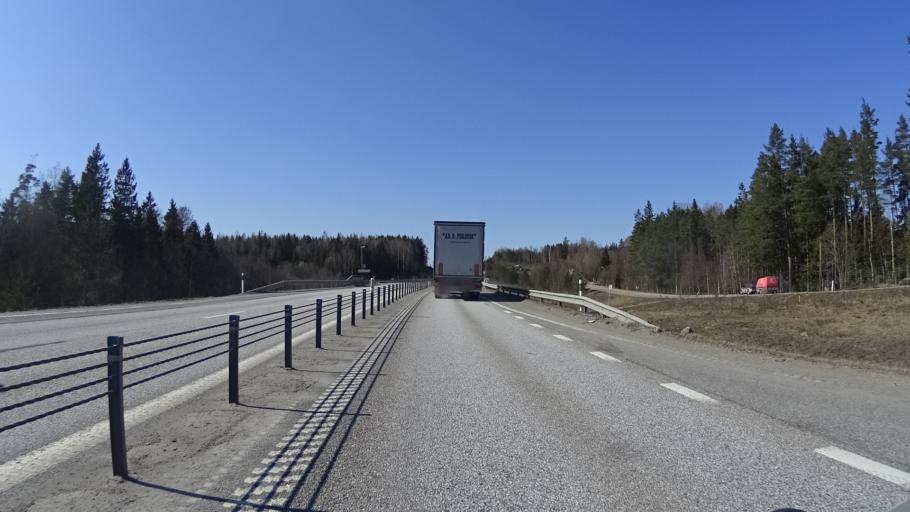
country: SE
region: OErebro
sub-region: Karlskoga Kommun
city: Karlskoga
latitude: 59.3235
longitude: 14.4524
